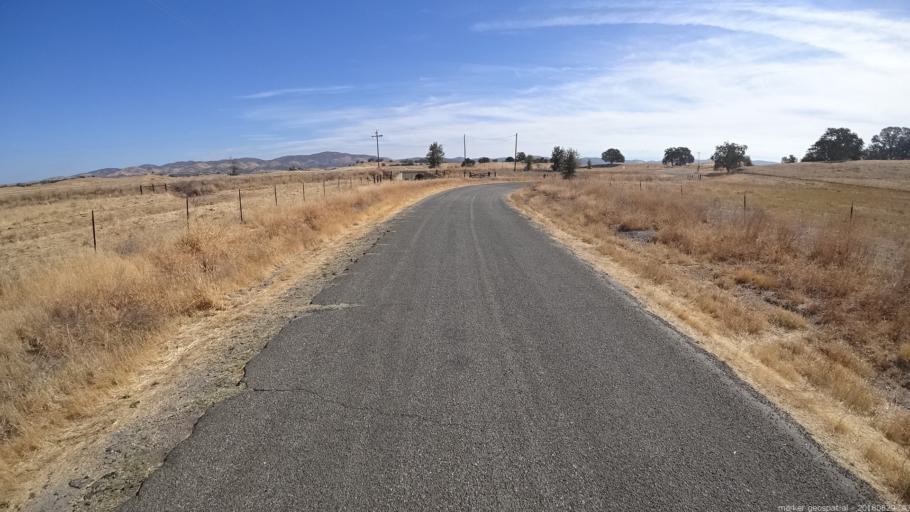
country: US
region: California
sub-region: Monterey County
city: King City
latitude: 35.9397
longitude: -121.1210
